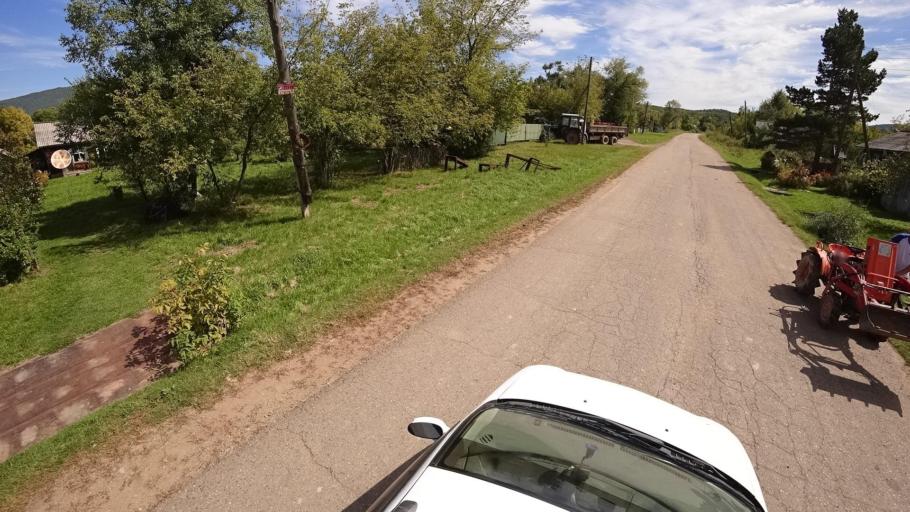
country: RU
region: Primorskiy
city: Yakovlevka
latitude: 44.6565
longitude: 133.7414
